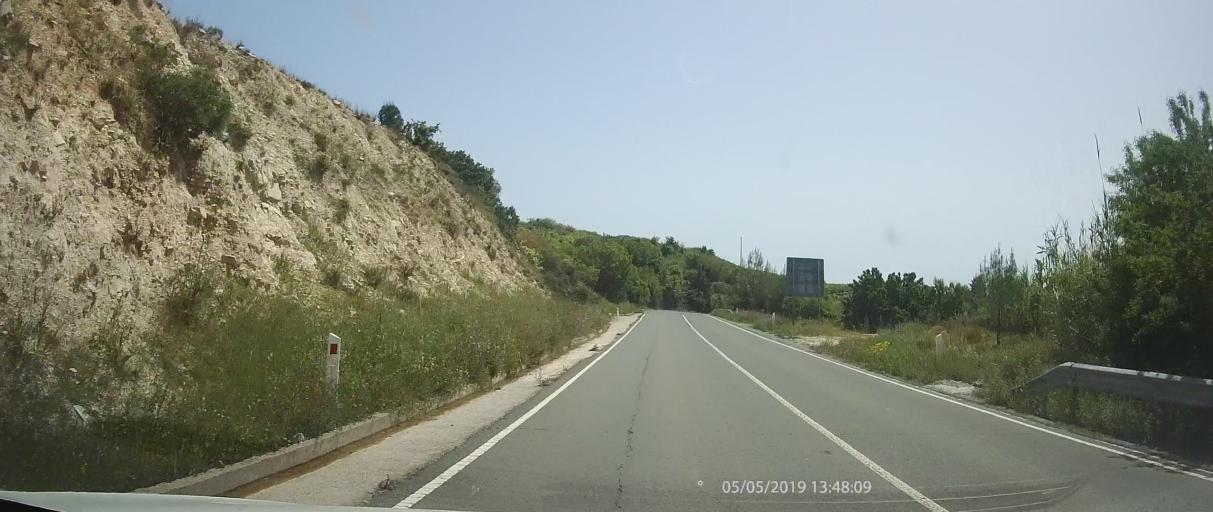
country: CY
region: Limassol
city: Pachna
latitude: 34.8596
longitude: 32.7558
